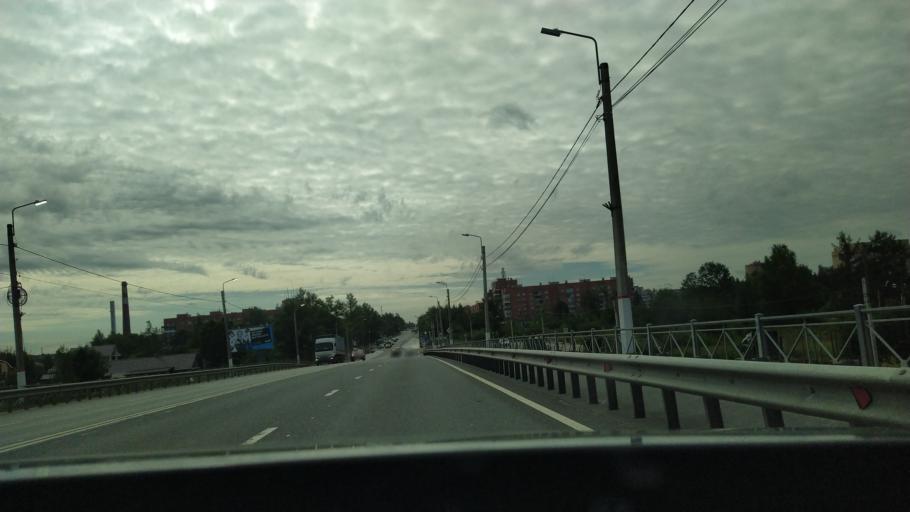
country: RU
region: Leningrad
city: Tosno
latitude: 59.5494
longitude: 30.8599
